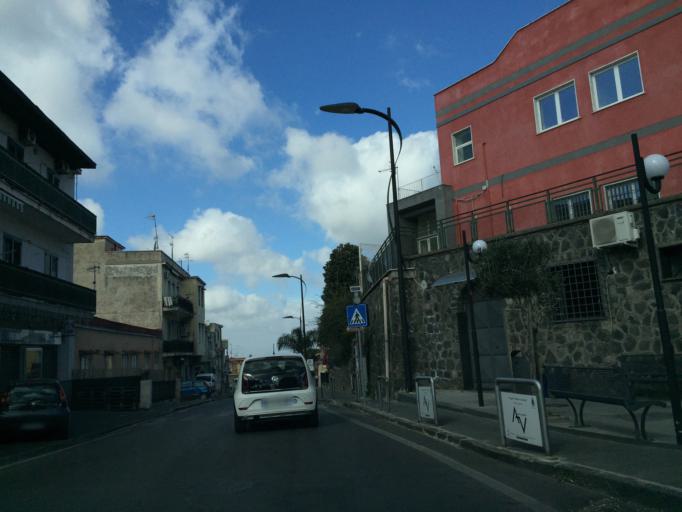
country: IT
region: Campania
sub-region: Provincia di Napoli
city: Massa di Somma
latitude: 40.8484
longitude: 14.3753
